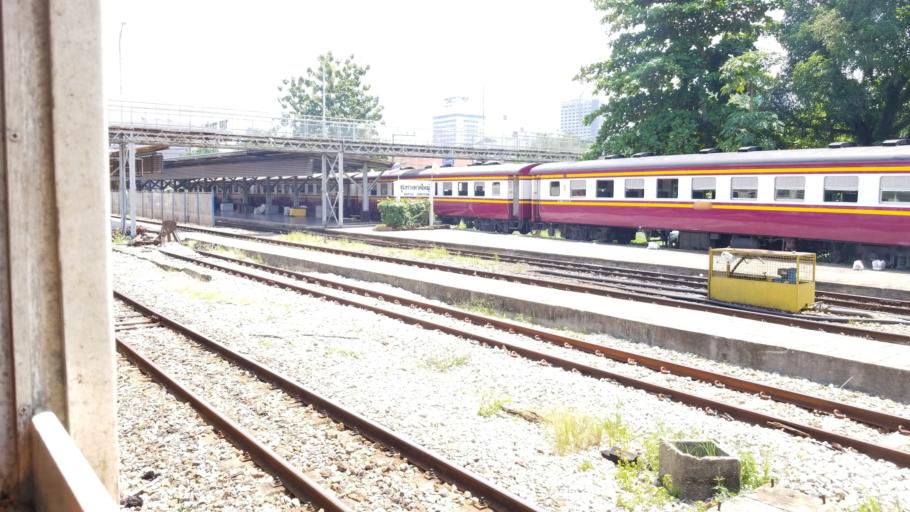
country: TH
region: Songkhla
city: Hat Yai
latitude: 7.0020
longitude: 100.4675
